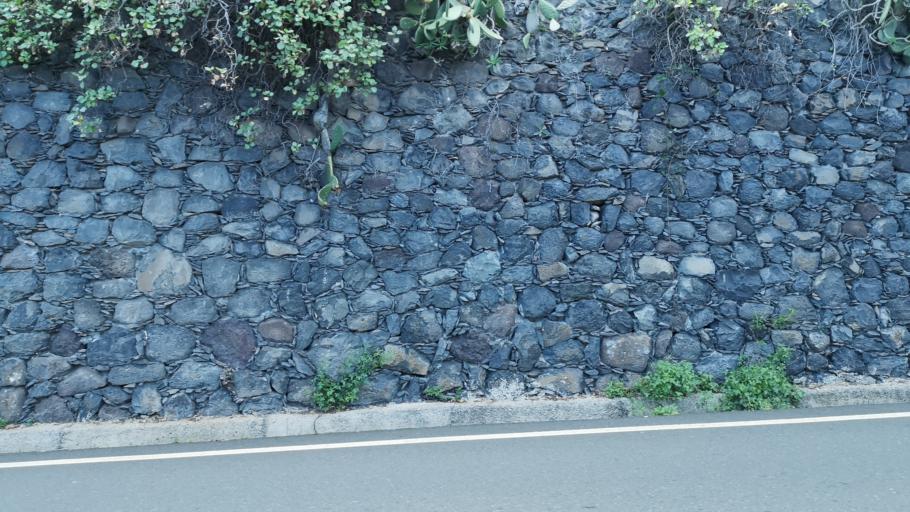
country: ES
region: Canary Islands
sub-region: Provincia de Santa Cruz de Tenerife
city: Agulo
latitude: 28.1855
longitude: -17.1913
